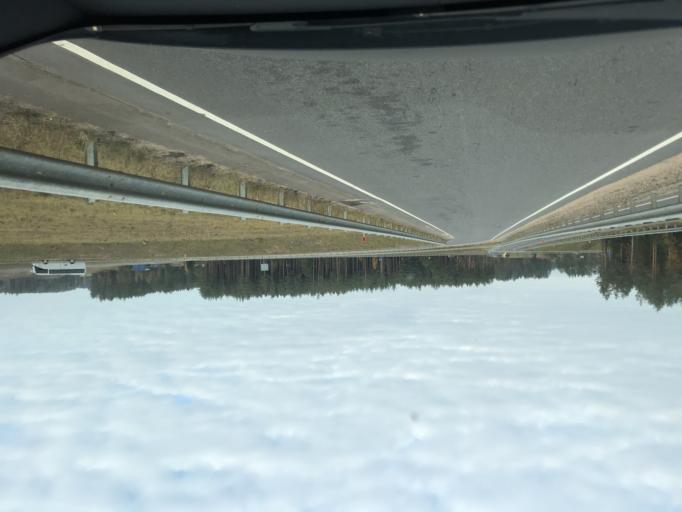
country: BY
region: Minsk
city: Rakaw
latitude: 53.9648
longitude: 27.0857
